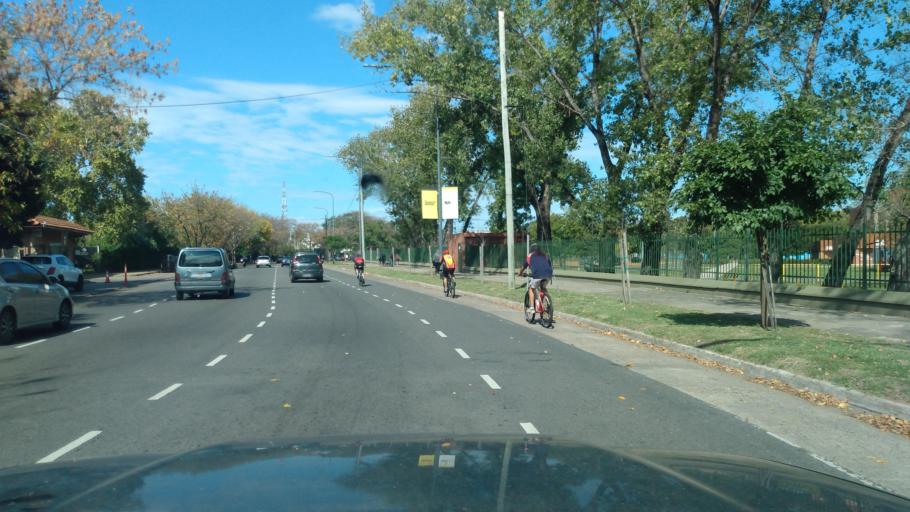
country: AR
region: Buenos Aires
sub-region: Partido de General San Martin
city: General San Martin
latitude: -34.5570
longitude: -58.4969
